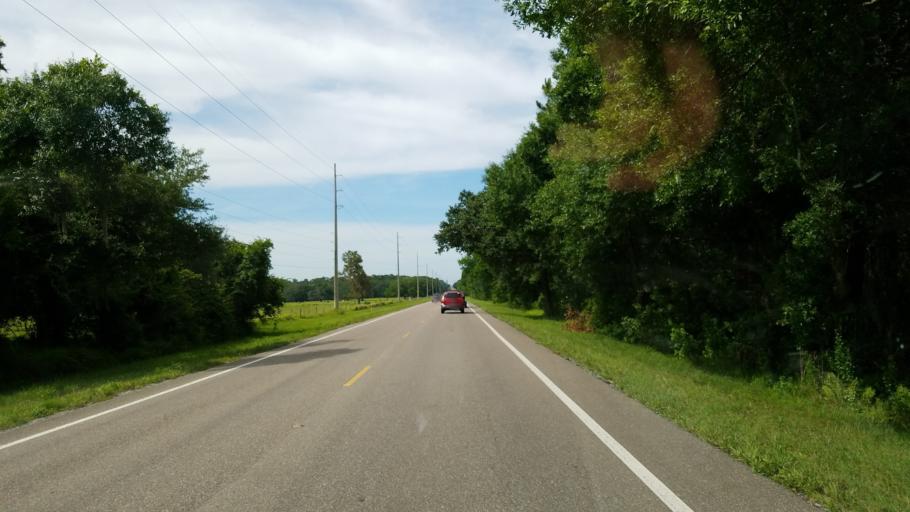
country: US
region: Florida
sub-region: Hillsborough County
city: Balm
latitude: 27.6804
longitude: -82.1462
